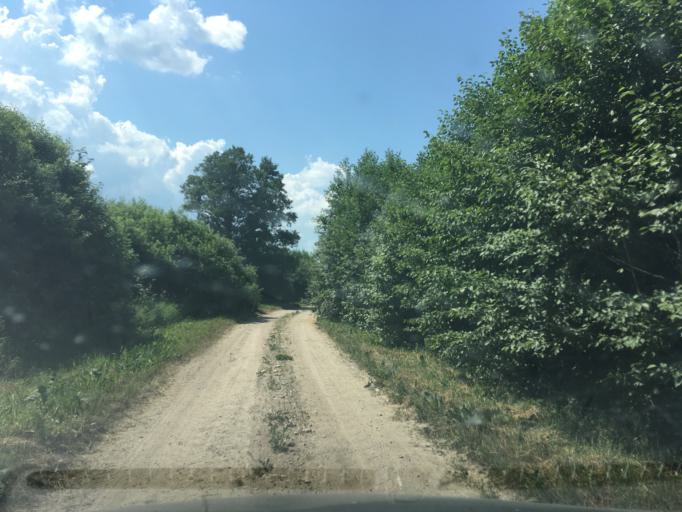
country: EE
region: Laeaene
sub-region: Lihula vald
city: Lihula
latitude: 58.7331
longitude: 24.1537
